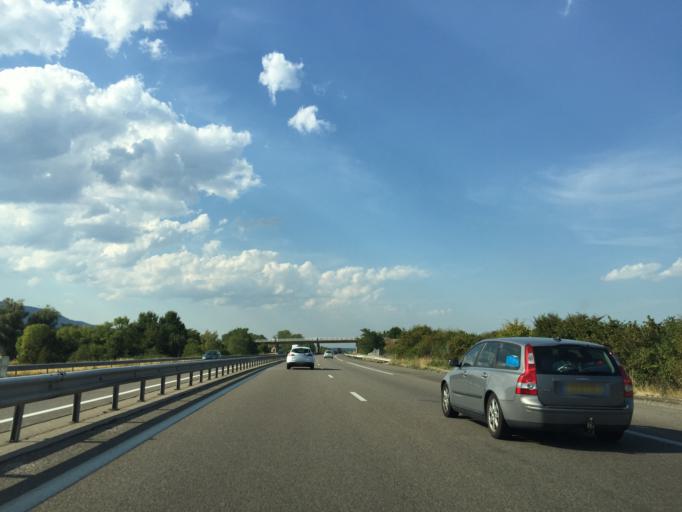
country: FR
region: Alsace
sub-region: Departement du Bas-Rhin
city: Stotzheim
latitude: 48.3749
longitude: 7.4808
